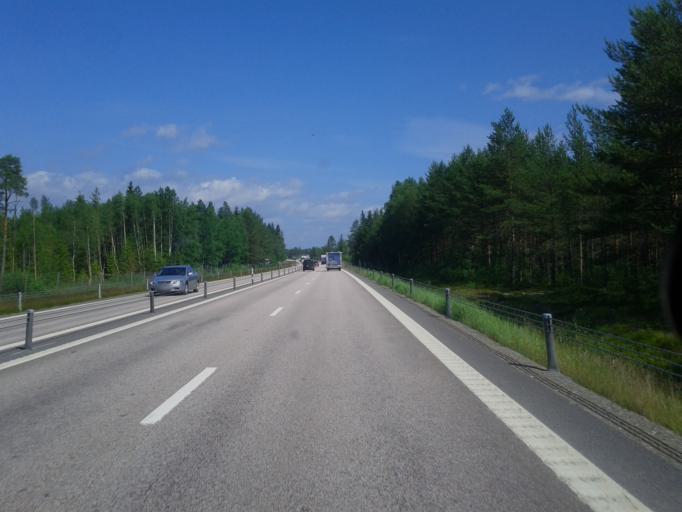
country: SE
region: Vaesterbotten
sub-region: Nordmalings Kommun
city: Nordmaling
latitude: 63.5281
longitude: 19.3913
